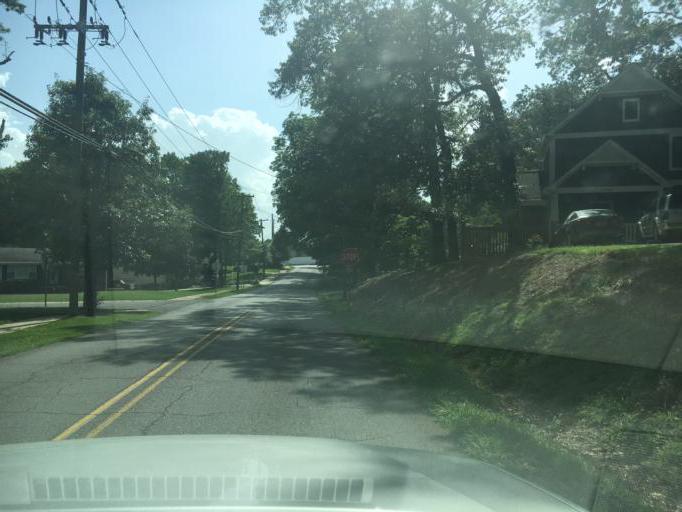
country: US
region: Alabama
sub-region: Jefferson County
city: Homewood
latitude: 33.4589
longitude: -86.8330
